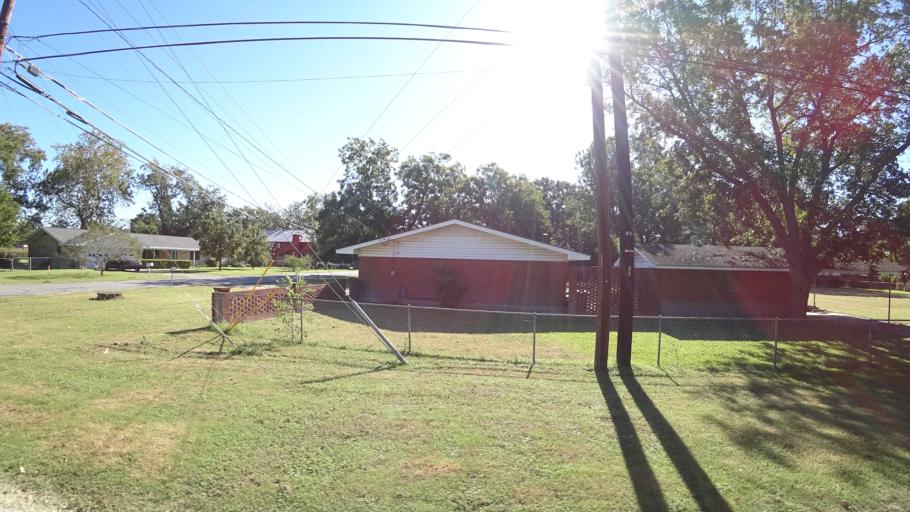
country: US
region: Texas
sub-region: Travis County
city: Manor
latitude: 30.3373
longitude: -97.6537
